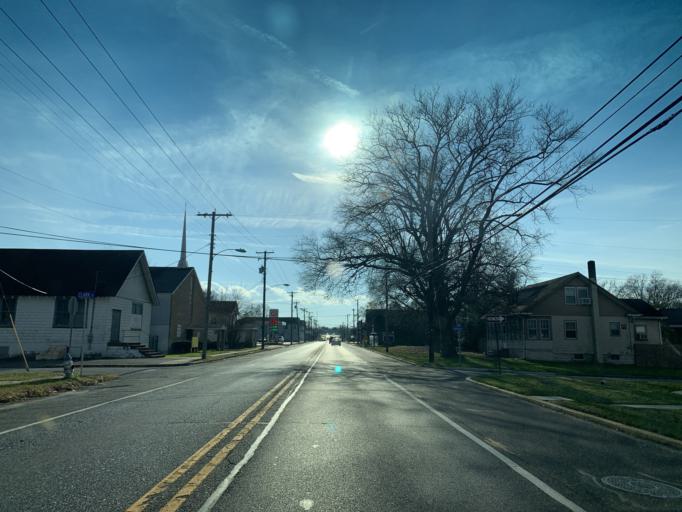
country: US
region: New Jersey
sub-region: Salem County
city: Carneys Point
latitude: 39.6847
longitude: -75.4897
